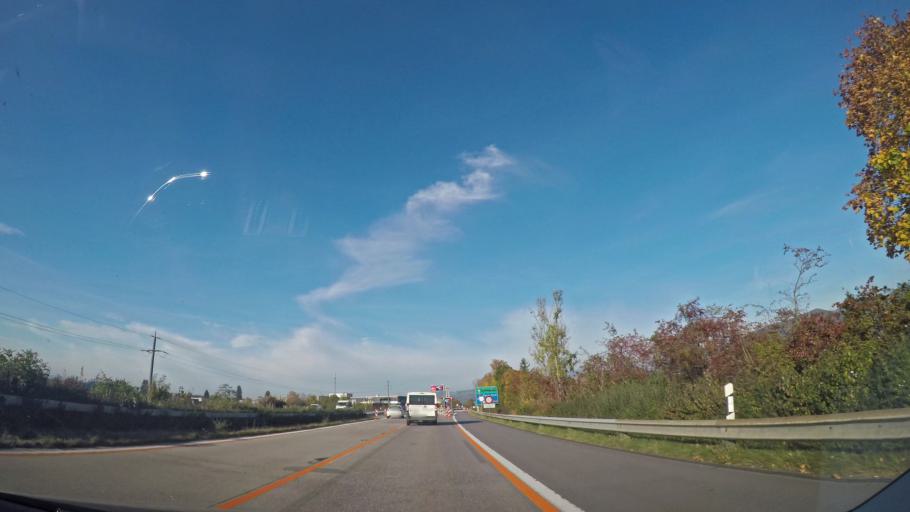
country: CH
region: Bern
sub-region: Thun District
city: Thun
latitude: 46.7371
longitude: 7.6008
